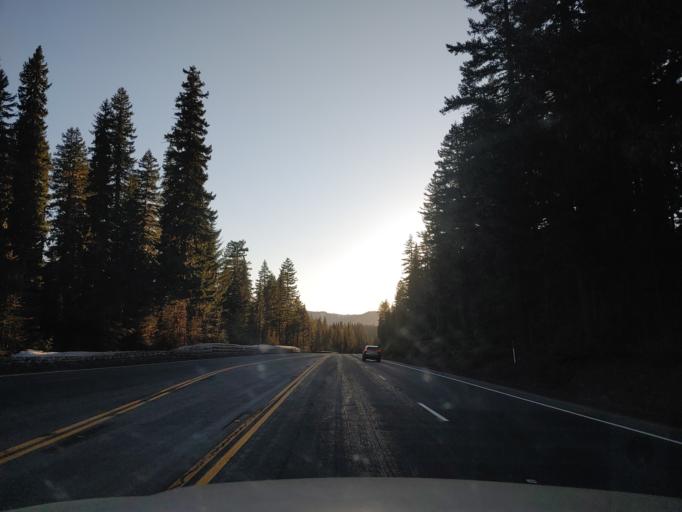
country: US
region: Oregon
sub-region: Lane County
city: Oakridge
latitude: 43.6173
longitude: -122.0849
